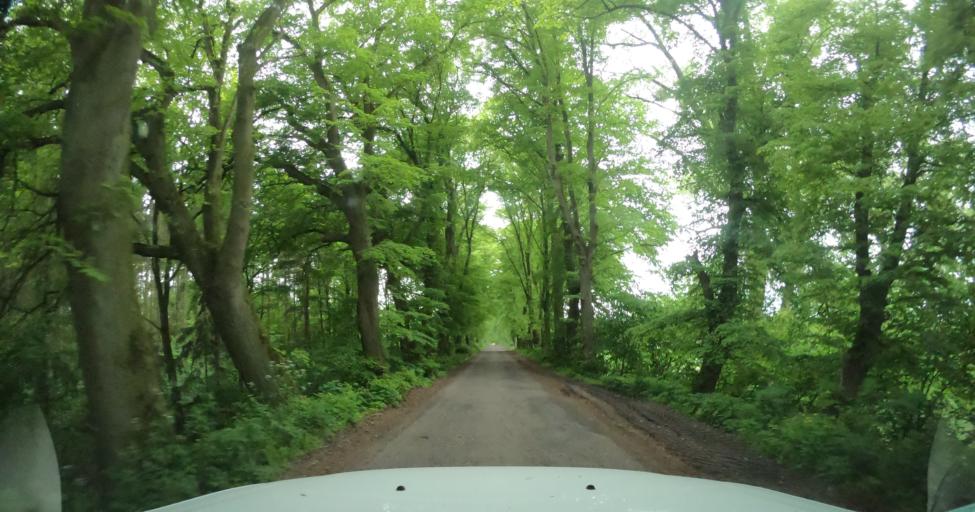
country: PL
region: West Pomeranian Voivodeship
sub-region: Powiat stargardzki
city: Dolice
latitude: 53.2429
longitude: 15.2445
